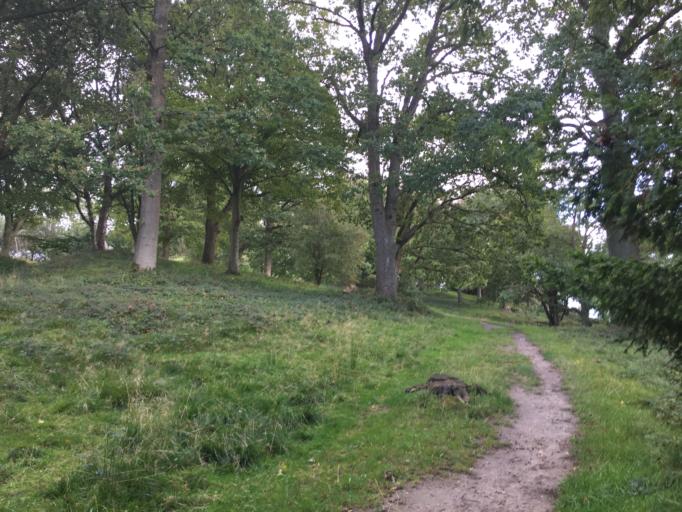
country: DK
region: South Denmark
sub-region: Assens Kommune
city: Vissenbjerg
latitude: 55.3391
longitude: 10.1147
